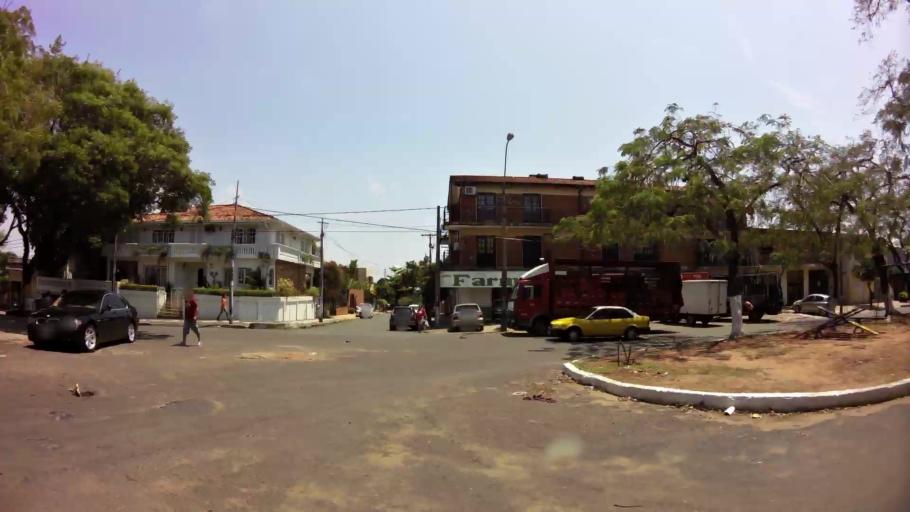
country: PY
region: Asuncion
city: Asuncion
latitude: -25.3028
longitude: -57.6371
